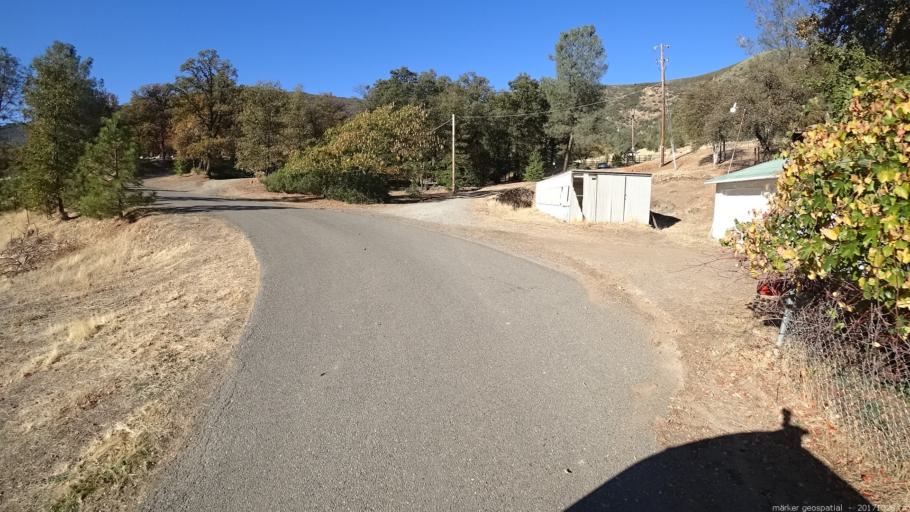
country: US
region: California
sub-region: Trinity County
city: Lewiston
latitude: 40.7038
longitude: -122.6380
